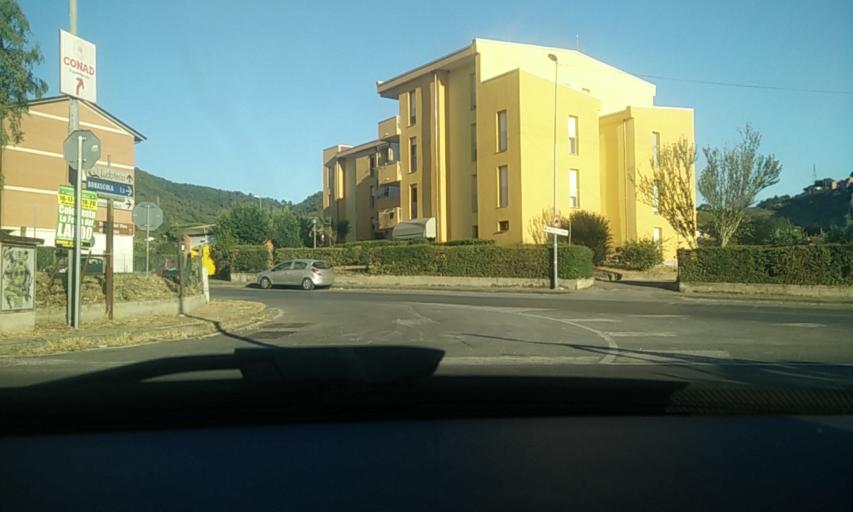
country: IT
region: Tuscany
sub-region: Provincia di Massa-Carrara
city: Carrara
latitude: 44.0597
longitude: 10.0807
